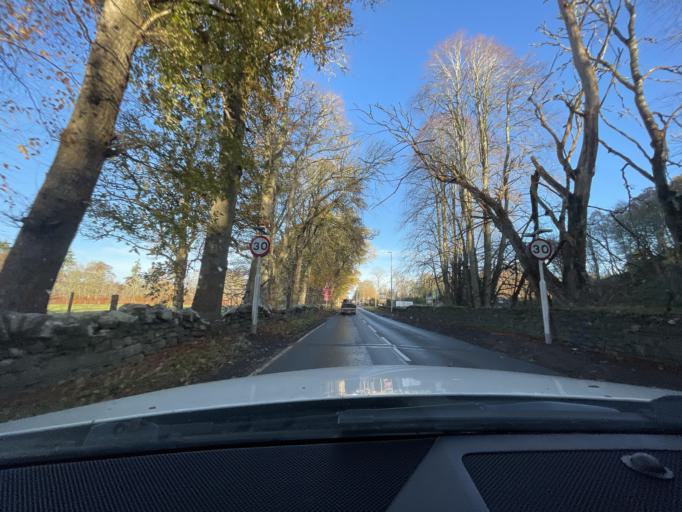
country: GB
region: Scotland
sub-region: Highland
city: Inverness
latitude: 57.4482
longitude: -4.2541
